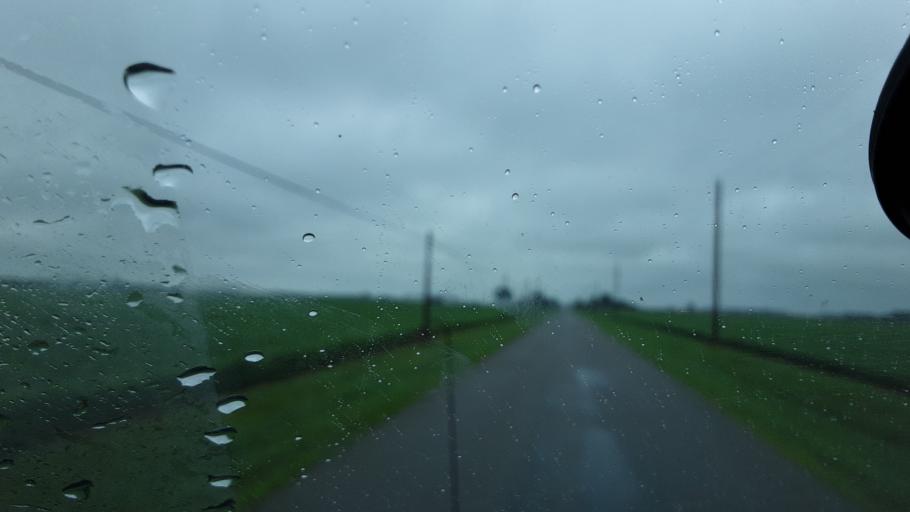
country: US
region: Ohio
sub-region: Mercer County
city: Rockford
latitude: 40.7566
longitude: -84.6409
